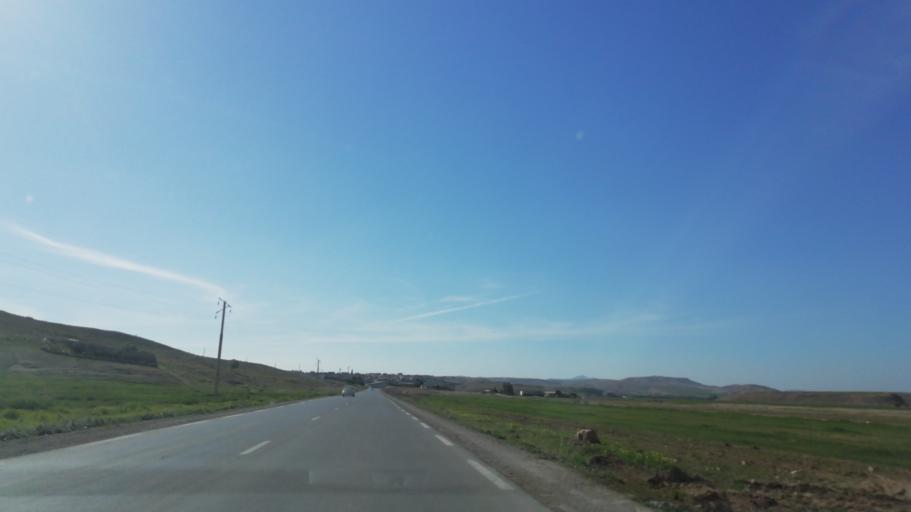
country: DZ
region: Mascara
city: Oued el Abtal
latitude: 35.4555
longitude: 0.7325
